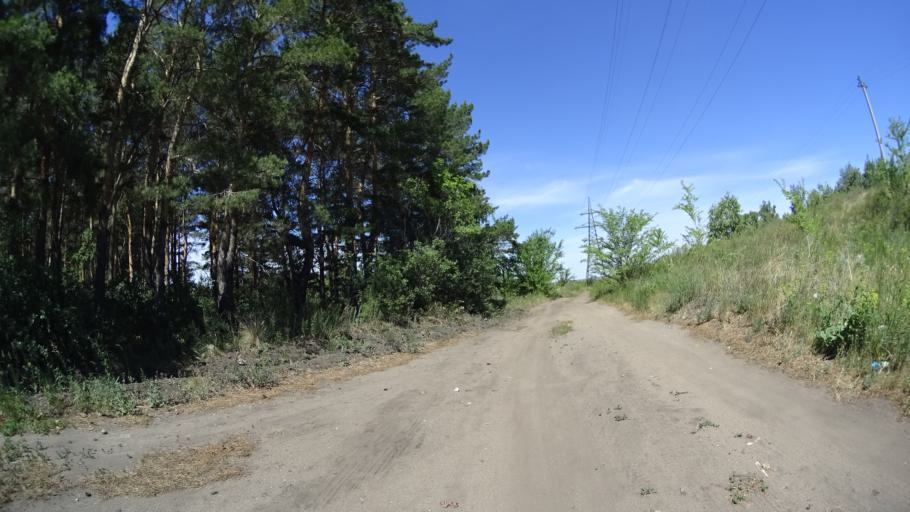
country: RU
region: Chelyabinsk
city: Troitsk
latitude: 54.0541
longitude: 61.6251
